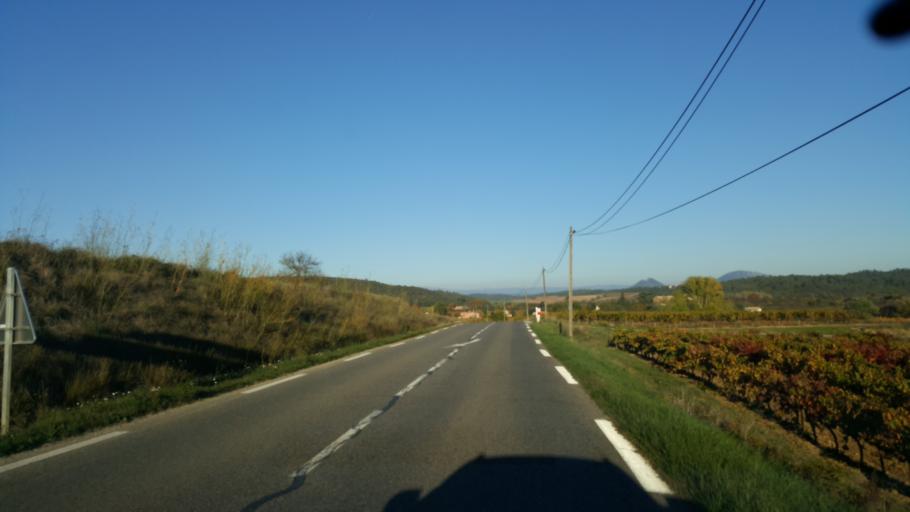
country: FR
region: Provence-Alpes-Cote d'Azur
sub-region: Departement du Var
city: Saint-Maximin-la-Sainte-Baume
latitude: 43.4925
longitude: 5.8908
